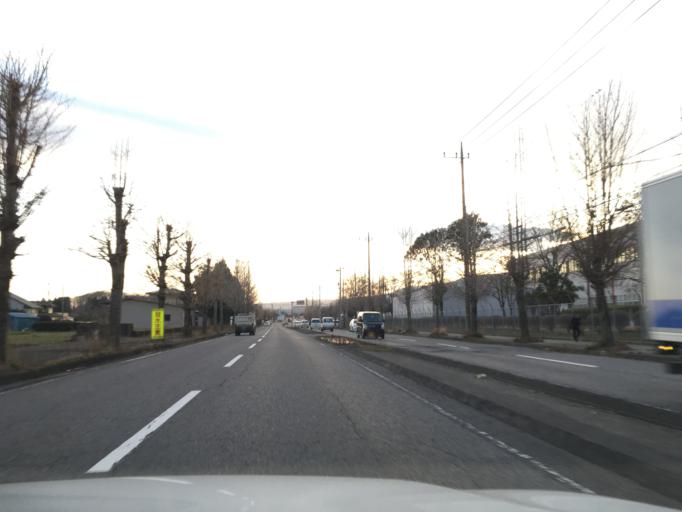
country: JP
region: Tochigi
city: Otawara
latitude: 36.9142
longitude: 139.9520
